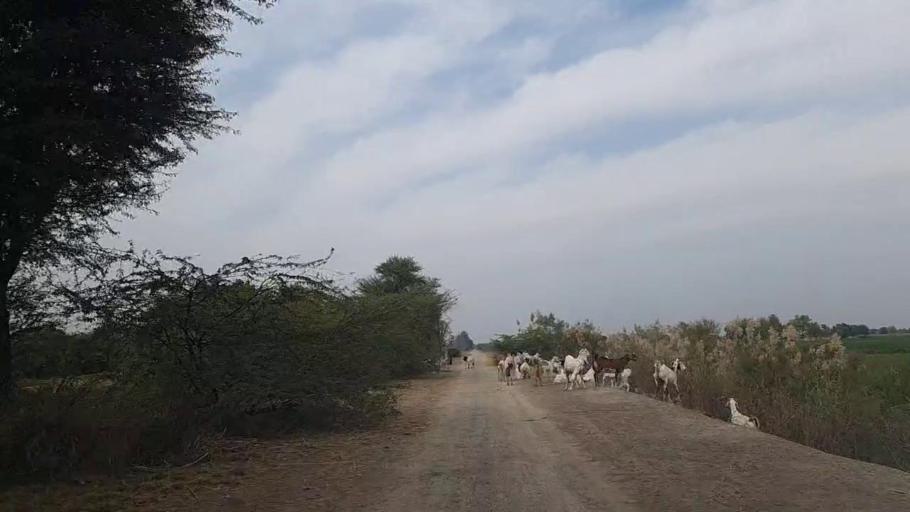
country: PK
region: Sindh
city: Daur
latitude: 26.4353
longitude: 68.4636
